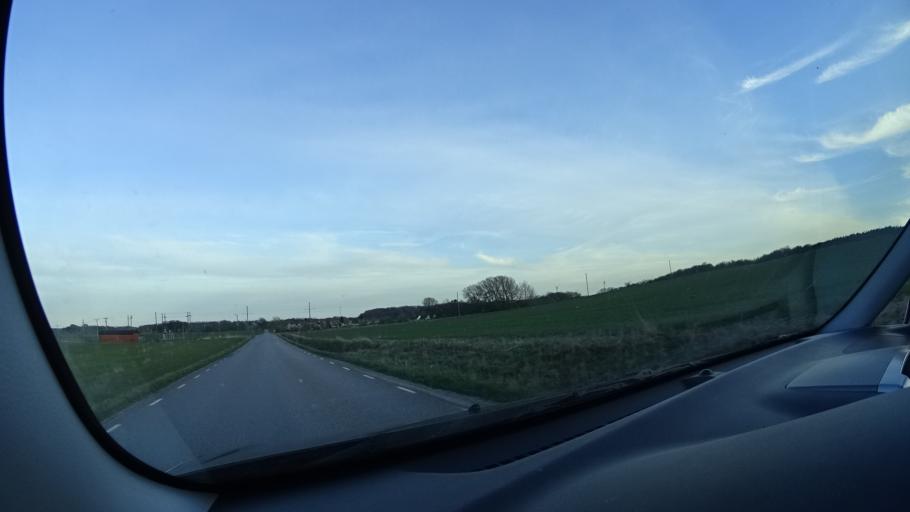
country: SE
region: Skane
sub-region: Eslovs Kommun
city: Stehag
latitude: 55.9104
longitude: 13.3915
